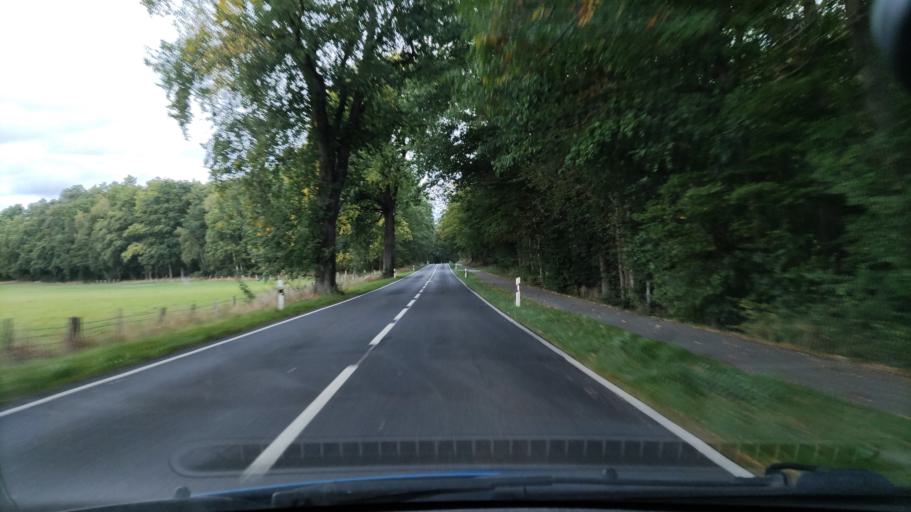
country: DE
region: Mecklenburg-Vorpommern
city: Lubtheen
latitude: 53.3772
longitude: 10.9663
